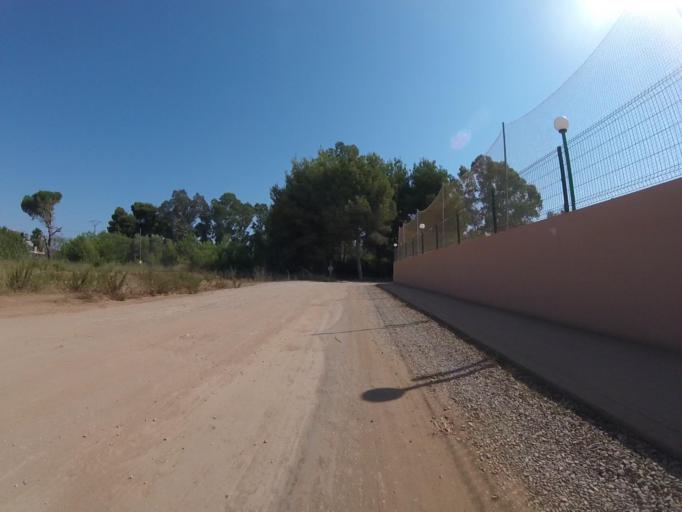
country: ES
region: Valencia
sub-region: Provincia de Castello
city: Orpesa/Oropesa del Mar
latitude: 40.1290
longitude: 0.1601
